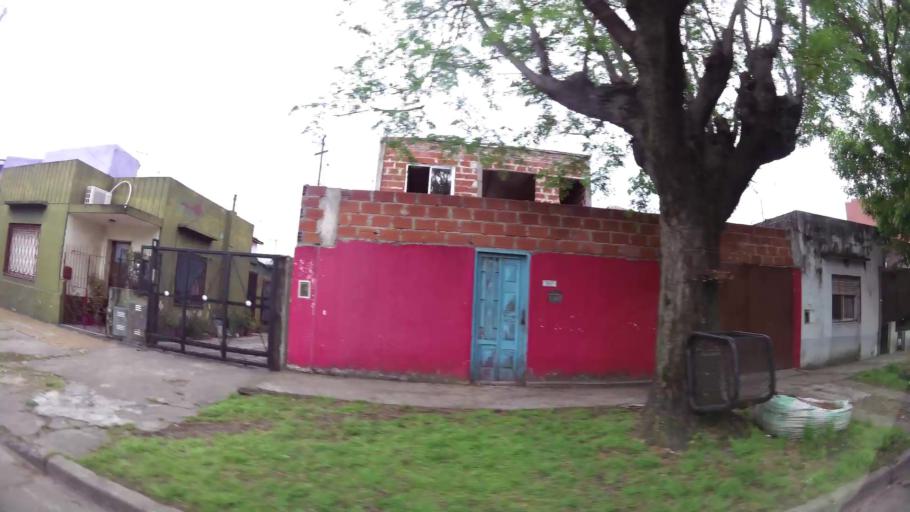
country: AR
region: Buenos Aires
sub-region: Partido de Quilmes
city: Quilmes
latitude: -34.7992
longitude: -58.2734
